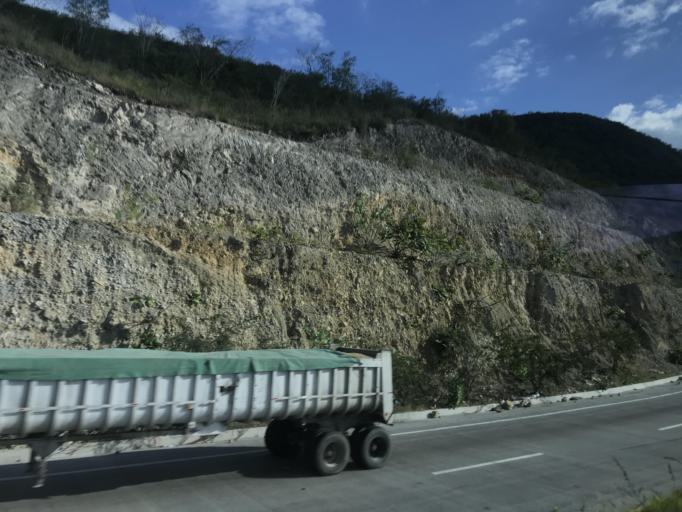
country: GT
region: El Progreso
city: Guastatoya
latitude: 14.8494
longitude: -90.1114
